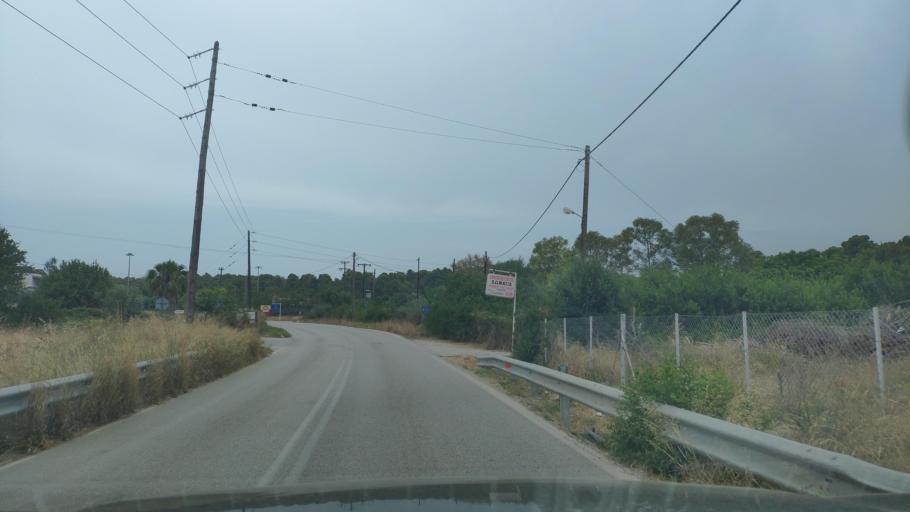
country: GR
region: Peloponnese
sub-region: Nomos Argolidos
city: Porto Cheli
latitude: 37.3124
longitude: 23.1581
